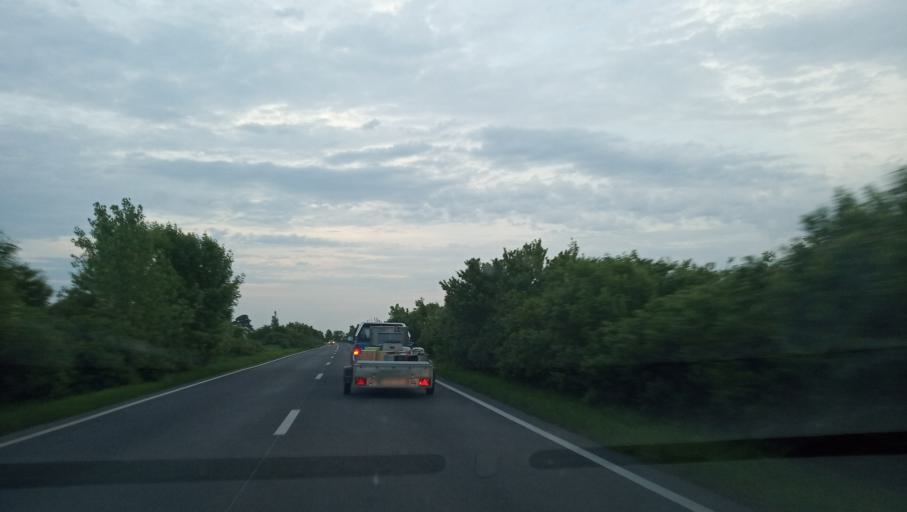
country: RO
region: Timis
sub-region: Comuna Voiteg
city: Voiteg
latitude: 45.5026
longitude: 21.2378
